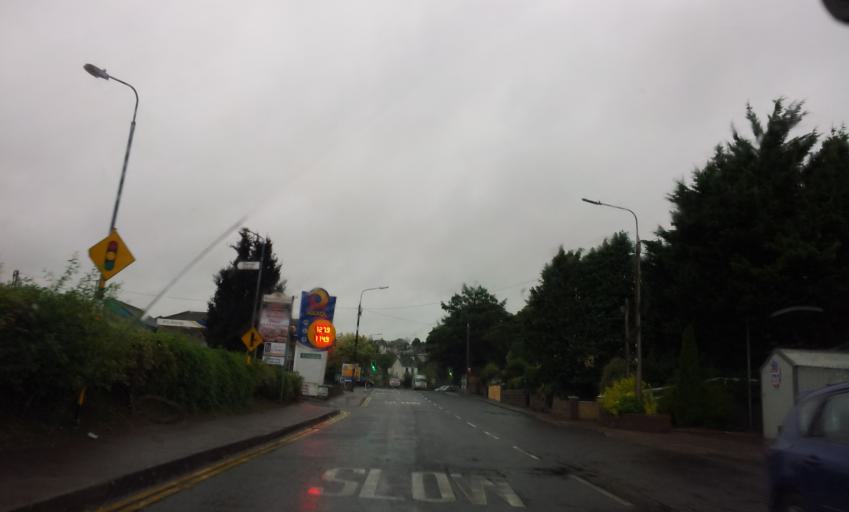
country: IE
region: Munster
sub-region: County Cork
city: Blarney
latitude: 51.9328
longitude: -8.5595
